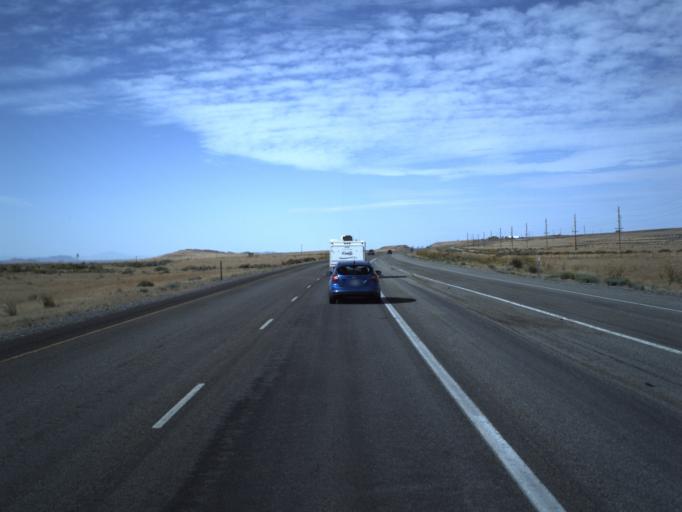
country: US
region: Utah
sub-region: Tooele County
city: Grantsville
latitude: 40.7667
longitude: -112.9898
